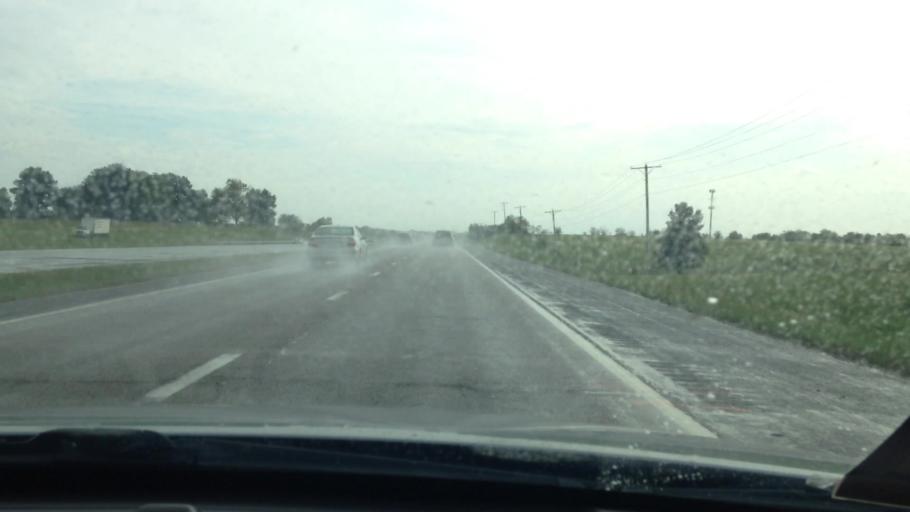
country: US
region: Kansas
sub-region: Leavenworth County
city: Basehor
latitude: 39.1576
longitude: -94.9008
